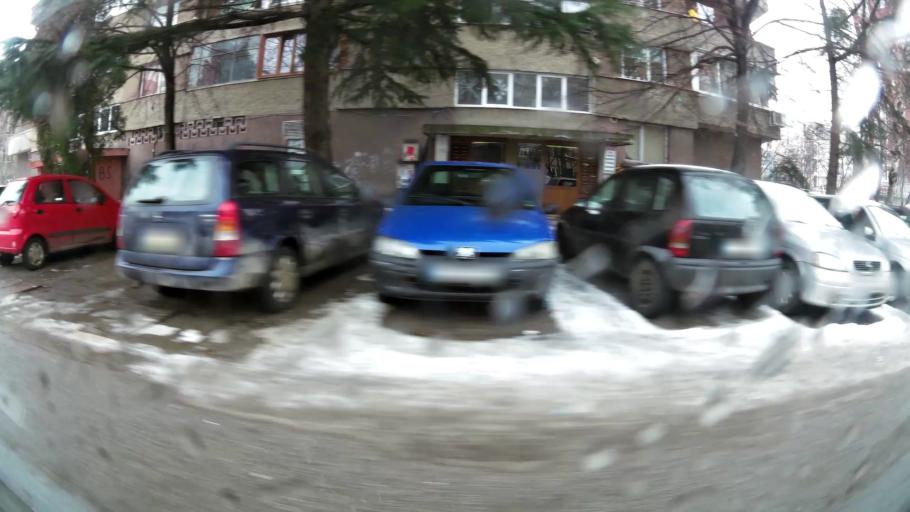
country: BG
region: Sofia-Capital
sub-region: Stolichna Obshtina
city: Sofia
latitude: 42.6741
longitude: 23.2860
